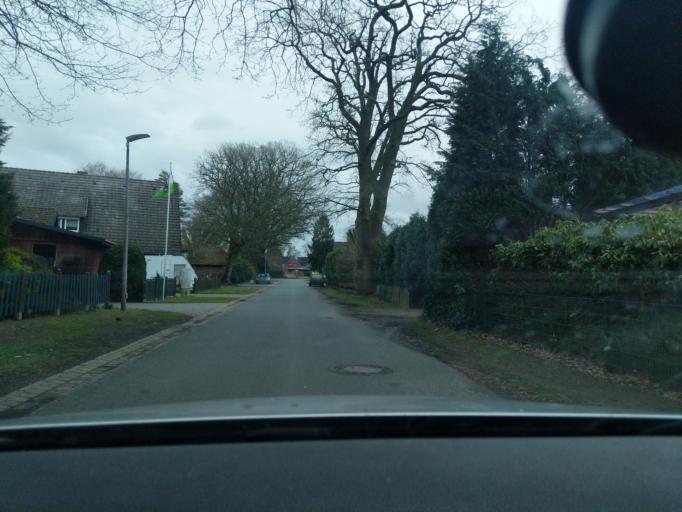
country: DE
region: Lower Saxony
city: Bremervorde
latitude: 53.4686
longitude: 9.1914
